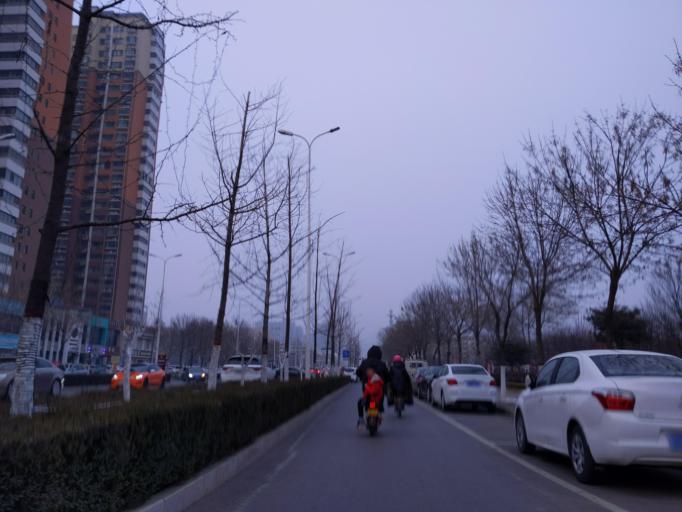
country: CN
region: Henan Sheng
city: Puyang
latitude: 35.7792
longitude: 115.0265
